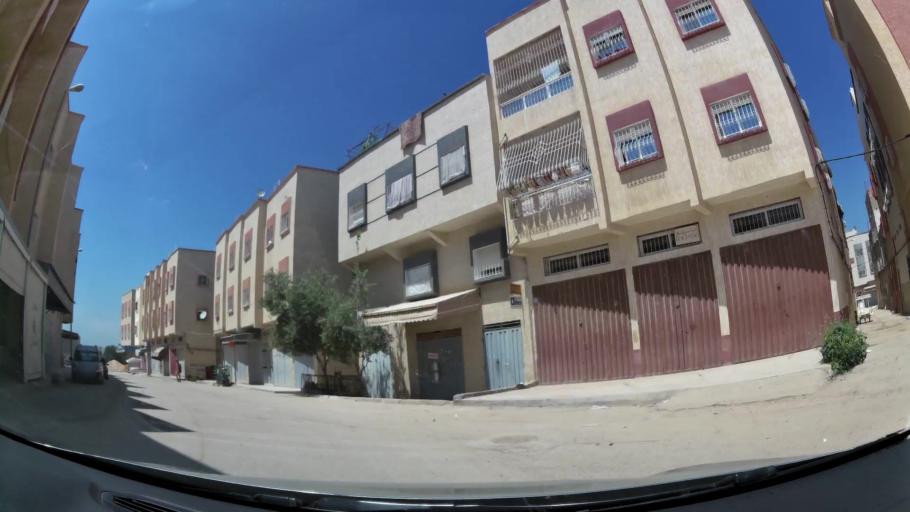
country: MA
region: Fes-Boulemane
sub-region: Fes
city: Fes
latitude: 34.0249
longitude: -5.0465
